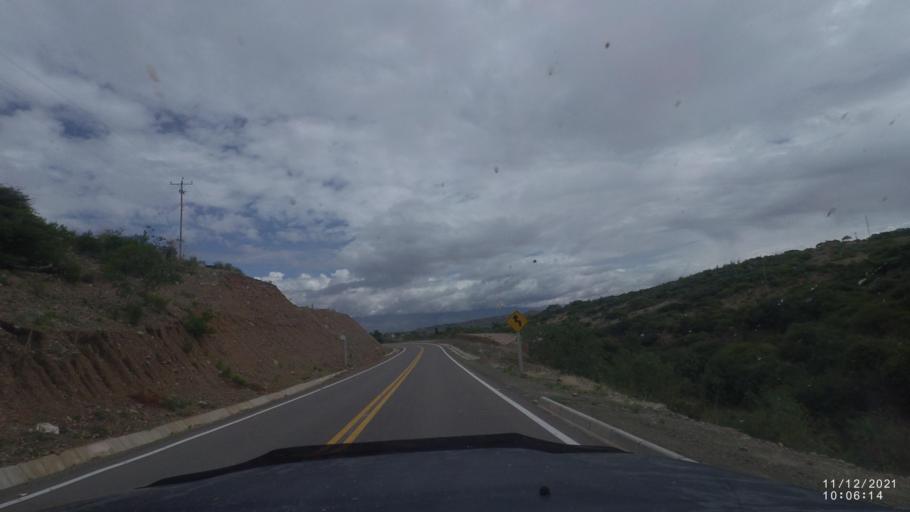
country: BO
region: Cochabamba
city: Cliza
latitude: -17.6912
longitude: -65.9489
